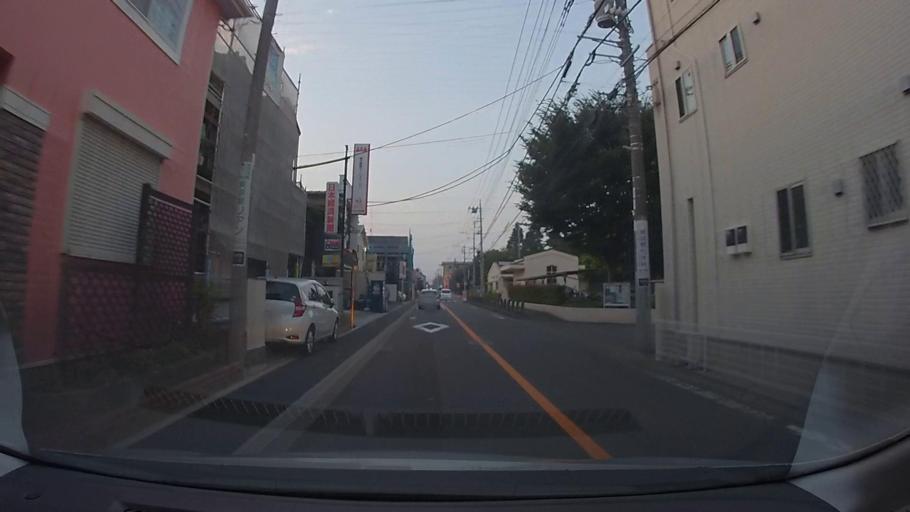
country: JP
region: Kanagawa
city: Minami-rinkan
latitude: 35.5025
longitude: 139.4429
